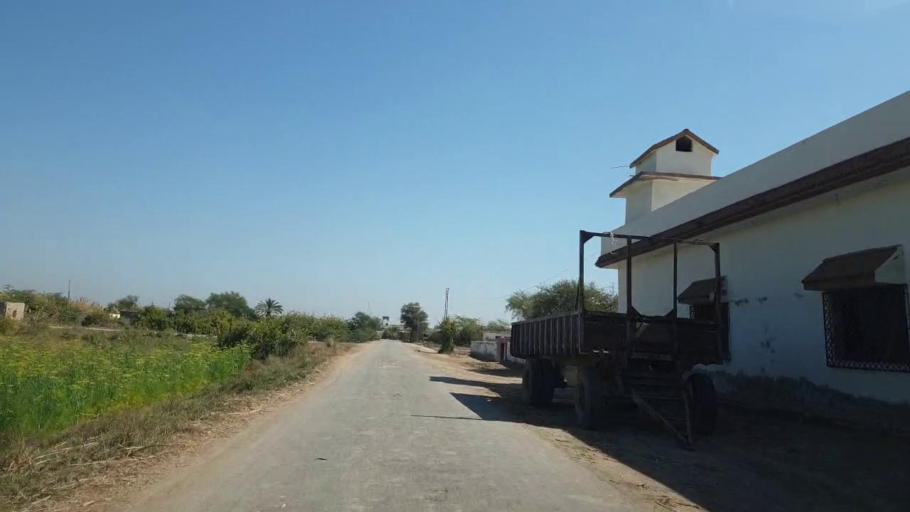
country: PK
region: Sindh
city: Mirpur Khas
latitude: 25.5965
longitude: 69.0921
